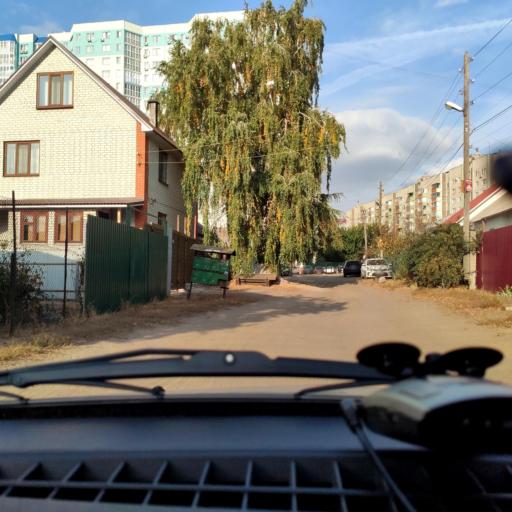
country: RU
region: Voronezj
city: Voronezh
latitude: 51.6526
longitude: 39.2377
